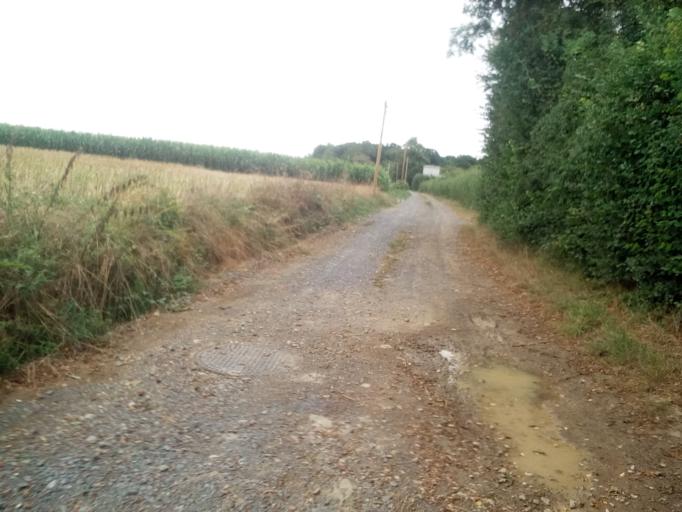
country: FR
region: Lower Normandy
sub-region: Departement du Calvados
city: Clinchamps-sur-Orne
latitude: 49.0618
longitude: -0.4180
